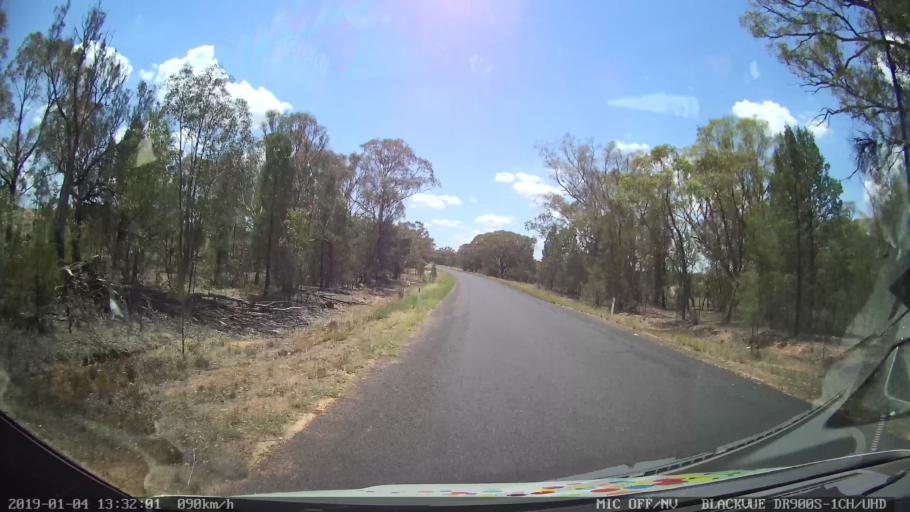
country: AU
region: New South Wales
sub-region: Dubbo Municipality
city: Eulomogo
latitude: -32.6150
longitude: 148.5490
